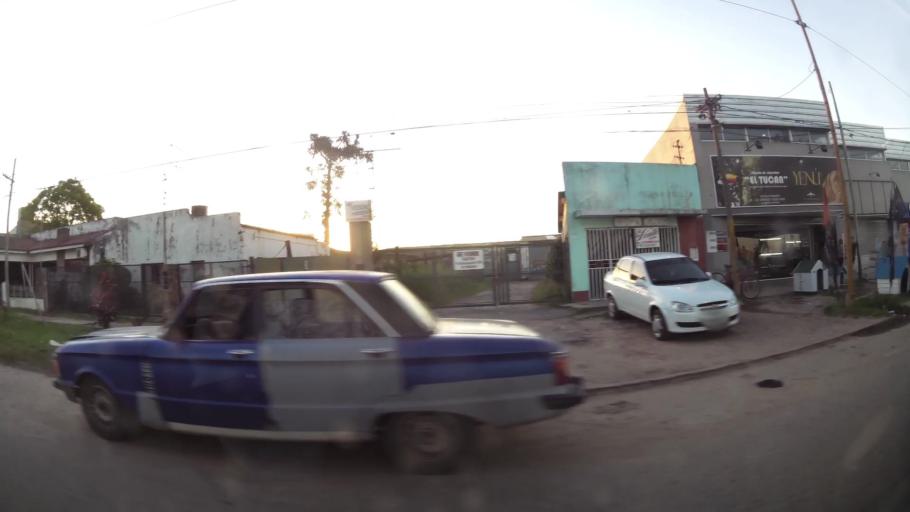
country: AR
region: Santa Fe
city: Santa Fe de la Vera Cruz
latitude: -31.5912
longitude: -60.6922
